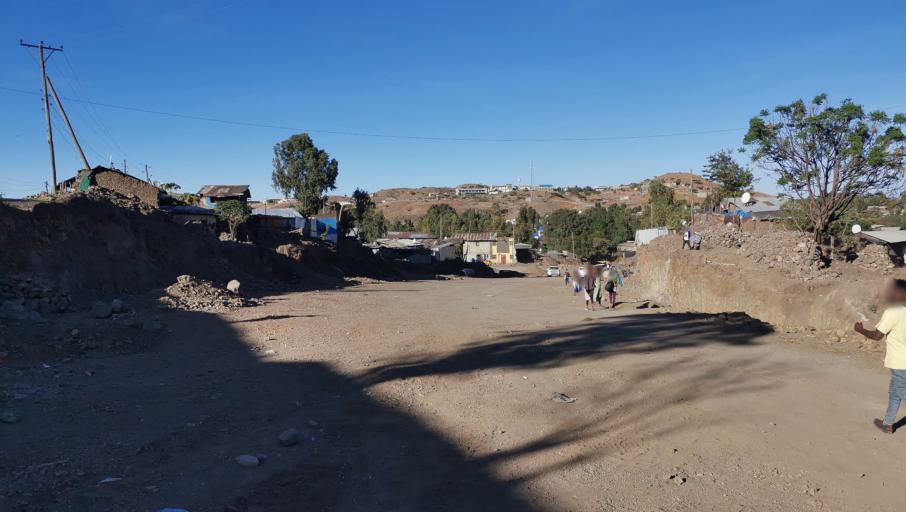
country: ET
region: Tigray
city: Korem
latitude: 12.6295
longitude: 39.0352
